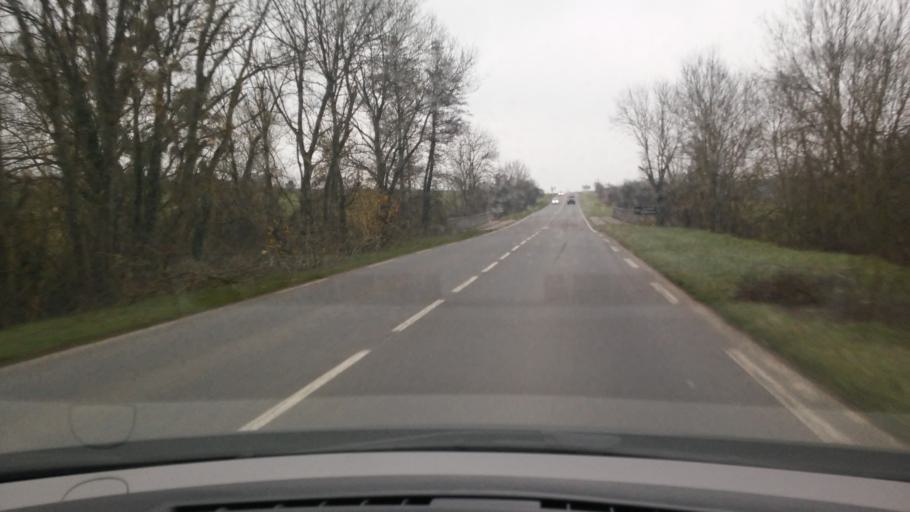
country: FR
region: Lorraine
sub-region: Departement de la Moselle
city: Courcelles-Chaussy
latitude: 49.0982
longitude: 6.4849
